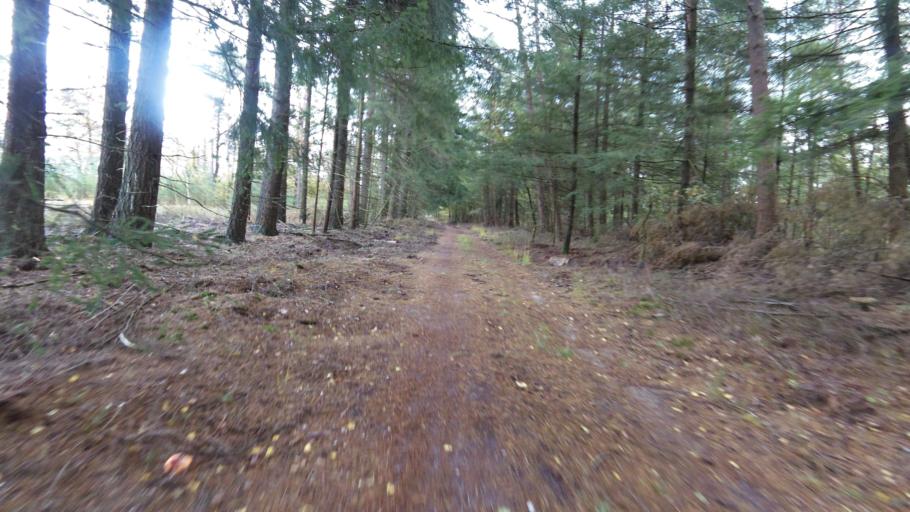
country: NL
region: Gelderland
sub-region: Gemeente Apeldoorn
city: Uddel
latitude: 52.3009
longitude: 5.8205
